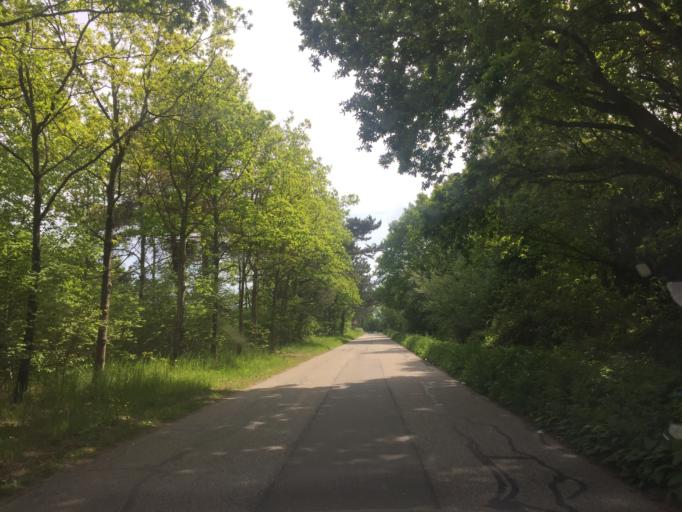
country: DK
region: South Denmark
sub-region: Nyborg Kommune
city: Nyborg
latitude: 55.2965
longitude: 10.8372
